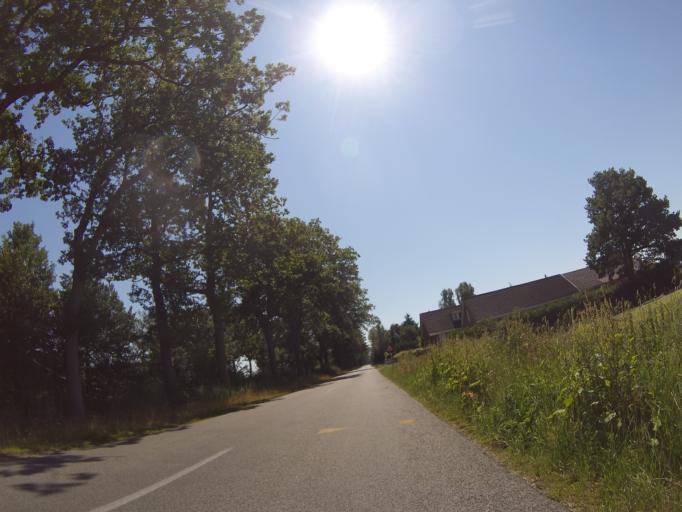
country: NL
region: Drenthe
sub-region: Gemeente Coevorden
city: Sleen
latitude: 52.8452
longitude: 6.7822
